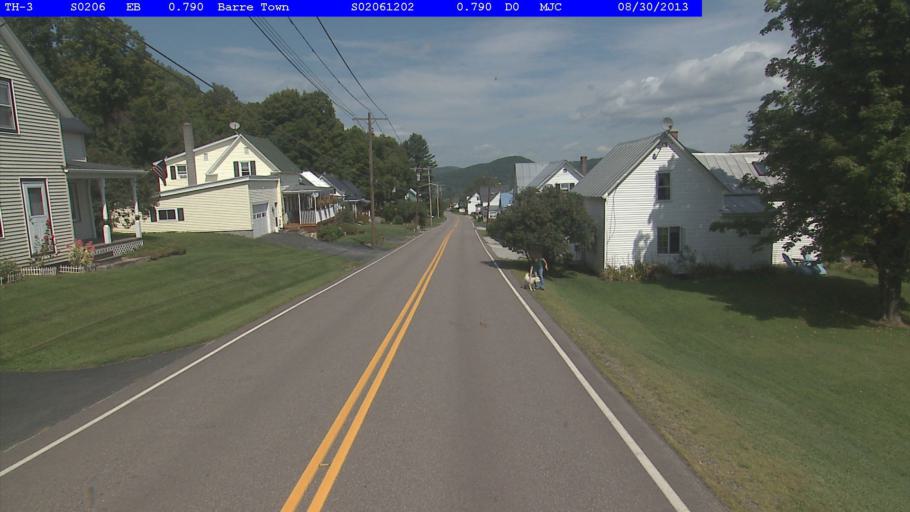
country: US
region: Vermont
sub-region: Washington County
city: South Barre
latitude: 44.1557
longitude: -72.4730
